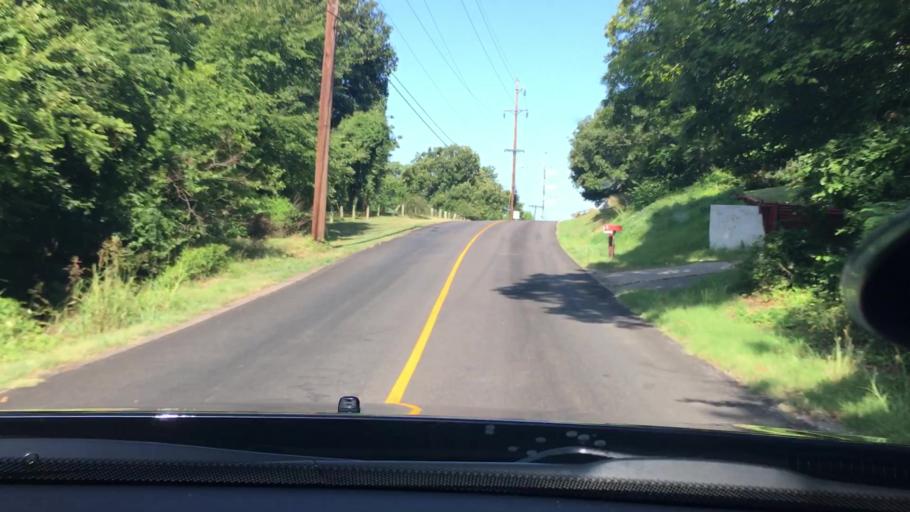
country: US
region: Oklahoma
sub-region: Pontotoc County
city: Ada
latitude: 34.7671
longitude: -96.6505
